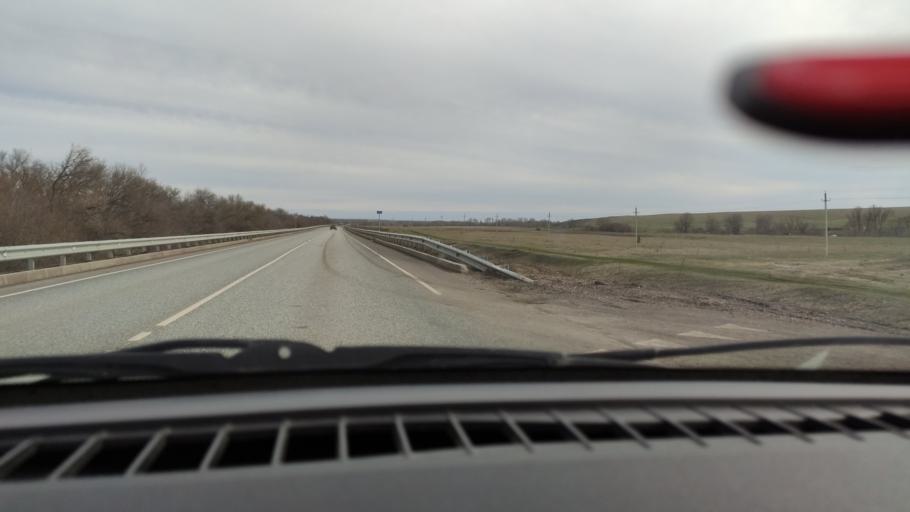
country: RU
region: Bashkortostan
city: Yermolayevo
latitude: 52.6069
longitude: 55.8465
